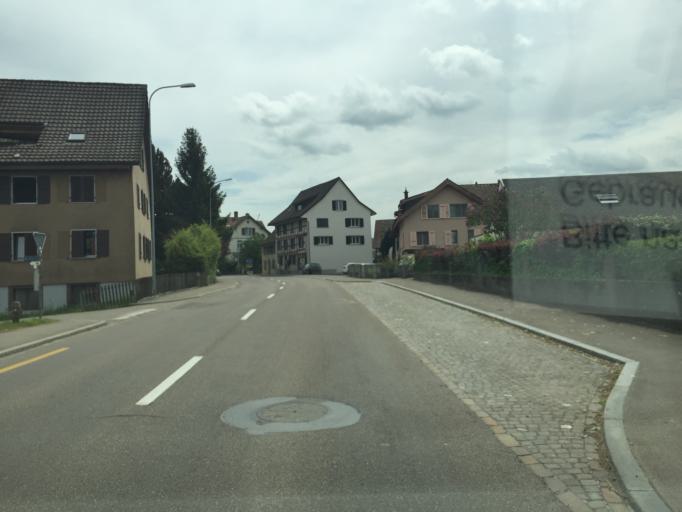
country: CH
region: Thurgau
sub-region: Frauenfeld District
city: Wagenhausen
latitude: 47.6587
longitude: 8.8511
